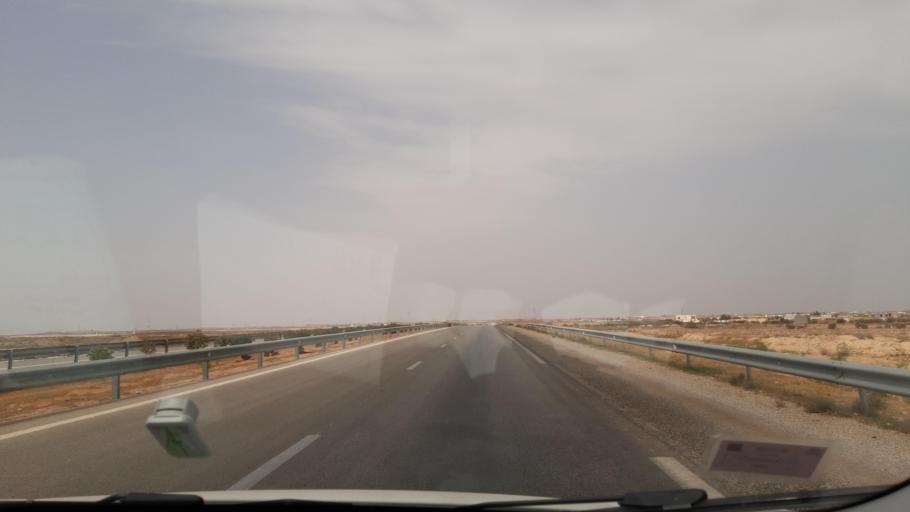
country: TN
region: Safaqis
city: Sfax
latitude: 34.7604
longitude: 10.6080
